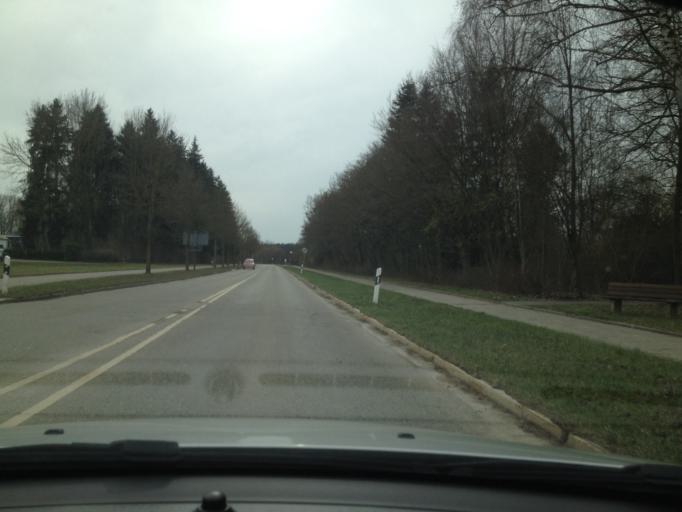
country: DE
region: Bavaria
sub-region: Swabia
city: Wehringen
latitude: 48.2740
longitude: 10.8041
